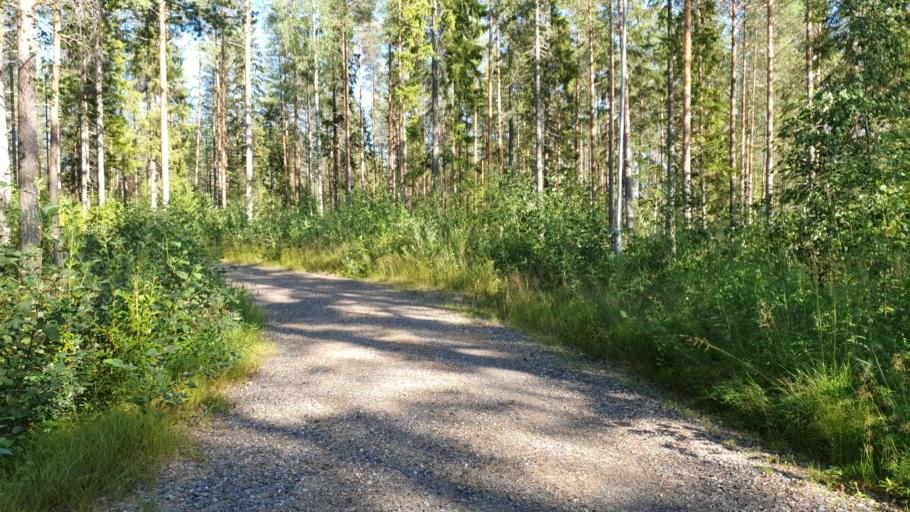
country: FI
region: Kainuu
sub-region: Kehys-Kainuu
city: Kuhmo
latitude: 64.1079
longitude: 29.5073
